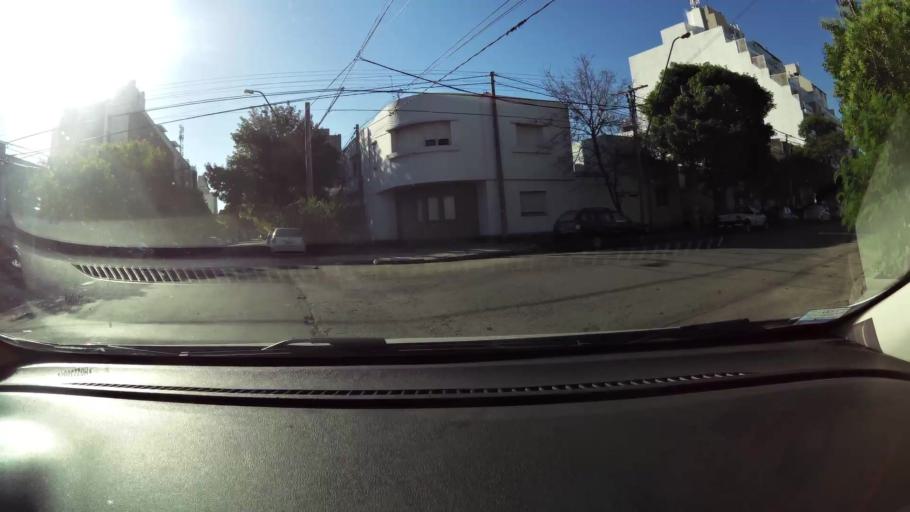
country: AR
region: Cordoba
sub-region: Departamento de Capital
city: Cordoba
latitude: -31.3939
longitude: -64.1835
